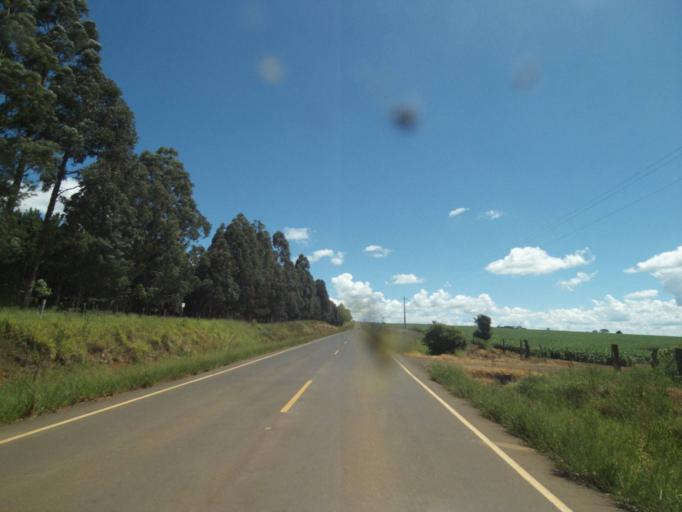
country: BR
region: Parana
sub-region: Pinhao
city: Pinhao
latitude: -25.8267
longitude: -52.0172
